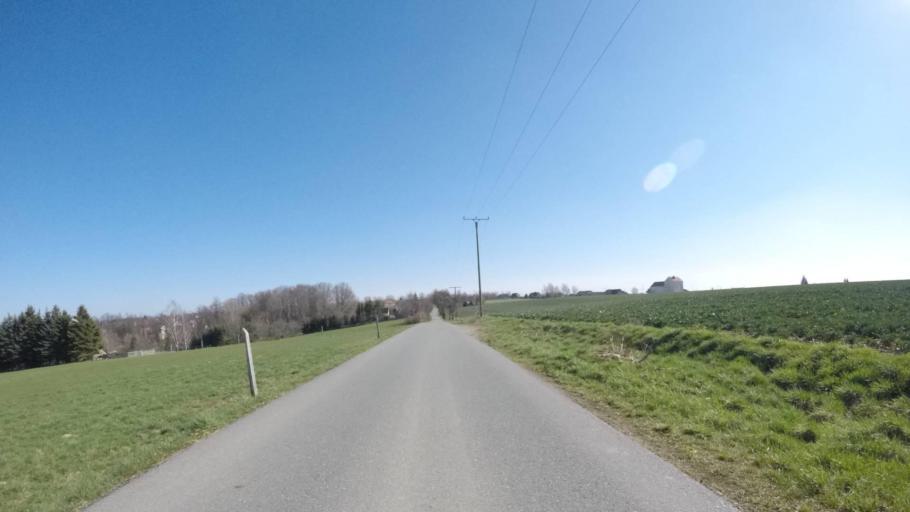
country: DE
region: Saxony
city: Niederfrohna
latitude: 50.8908
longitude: 12.6746
